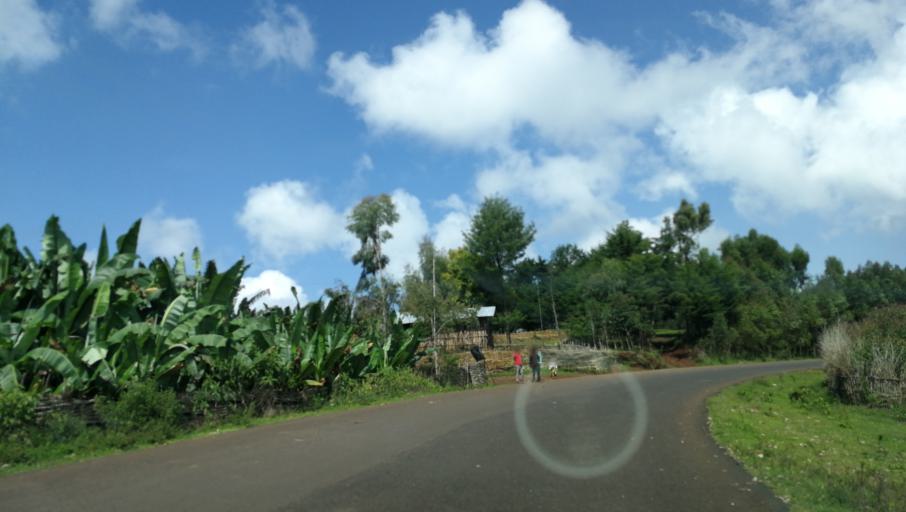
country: ET
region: Southern Nations, Nationalities, and People's Region
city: Areka
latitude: 7.0275
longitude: 37.2133
